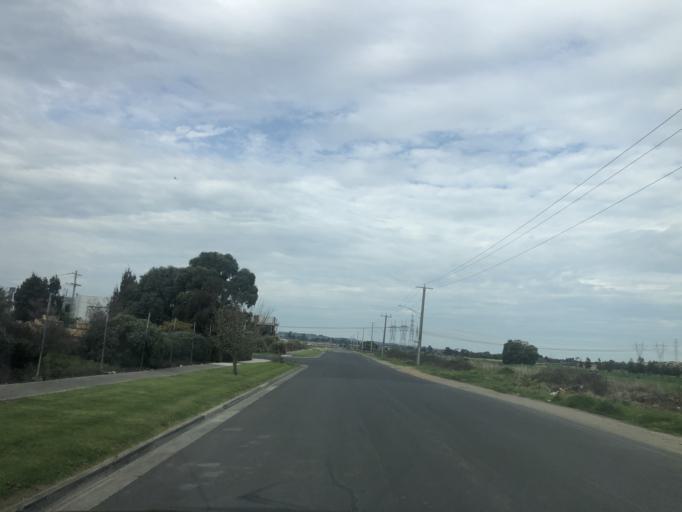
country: AU
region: Victoria
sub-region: Casey
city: Hallam
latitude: -38.0207
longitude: 145.2781
